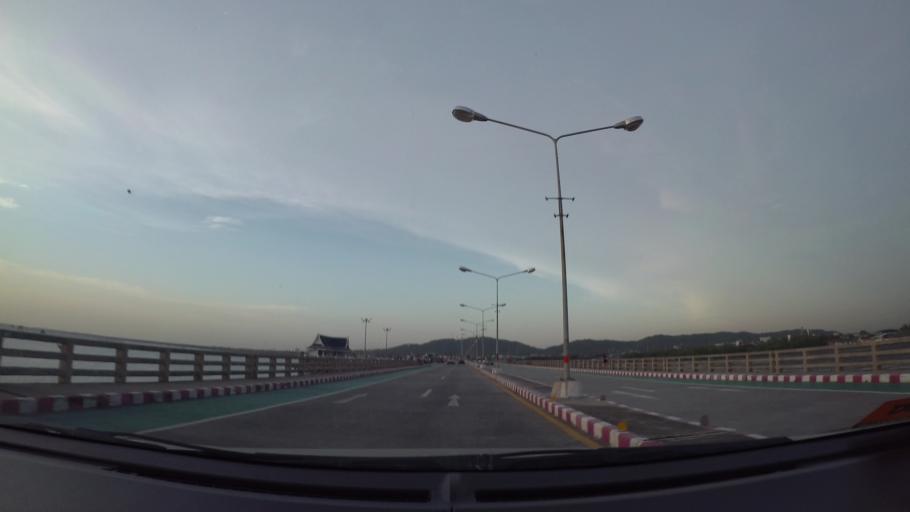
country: TH
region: Chon Buri
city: Chon Buri
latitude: 13.3768
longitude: 100.9791
